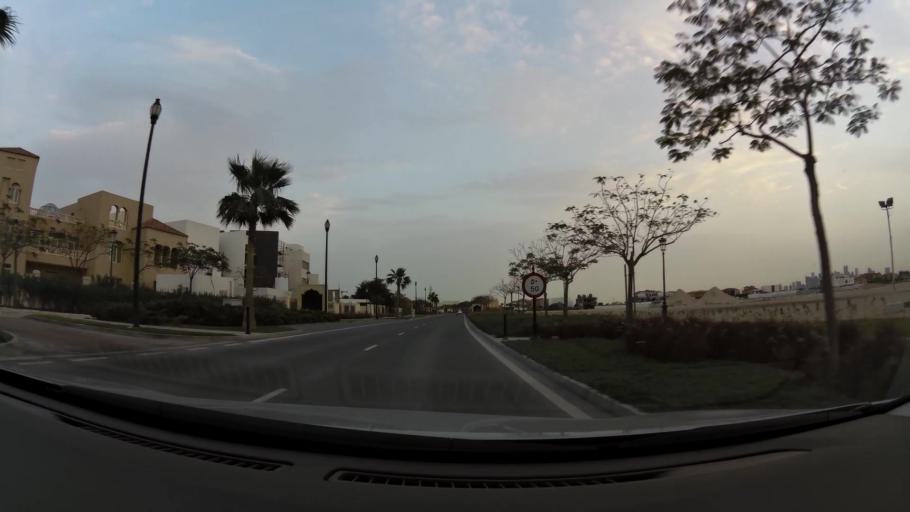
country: QA
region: Baladiyat ad Dawhah
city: Doha
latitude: 25.3658
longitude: 51.5640
